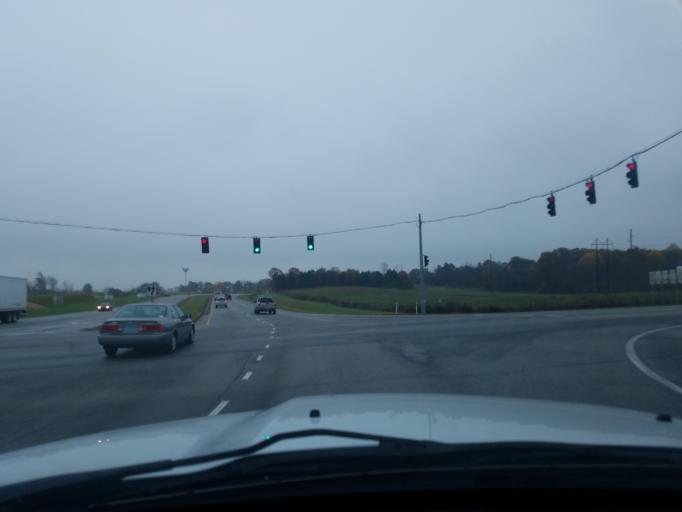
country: US
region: Kentucky
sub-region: Hardin County
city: Elizabethtown
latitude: 37.6701
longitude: -85.8469
